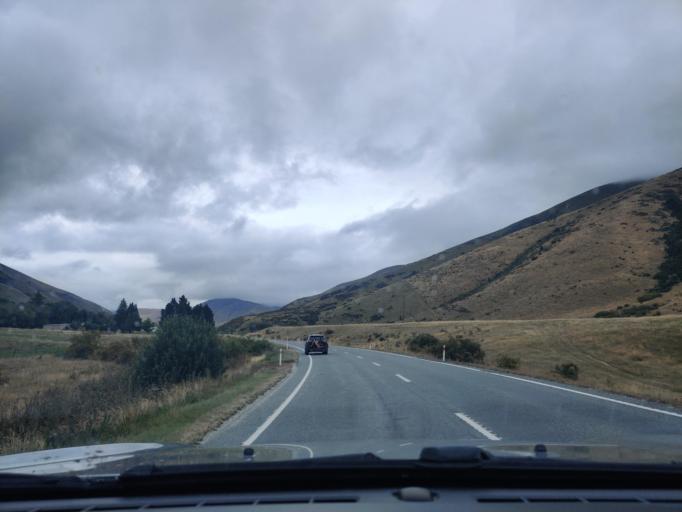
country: NZ
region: Otago
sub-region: Queenstown-Lakes District
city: Wanaka
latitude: -44.4978
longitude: 169.7565
